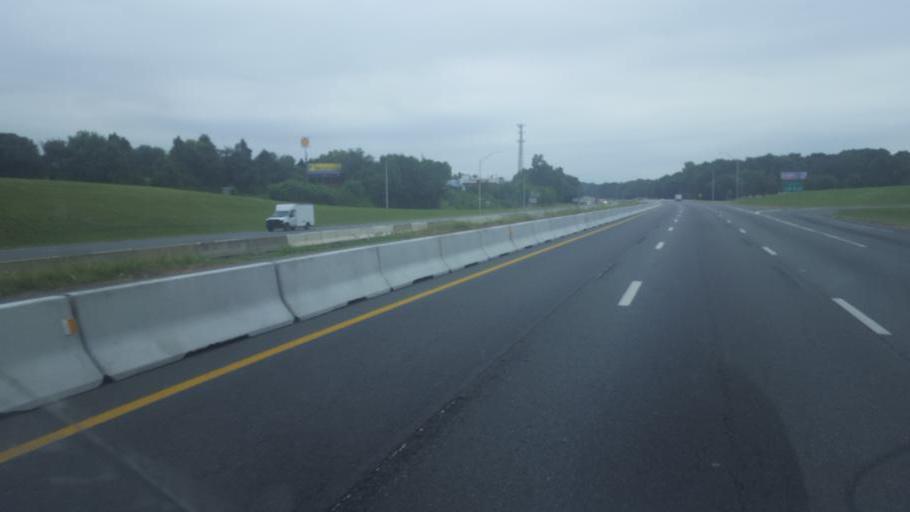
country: US
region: North Carolina
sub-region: Mecklenburg County
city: Charlotte
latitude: 35.3077
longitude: -80.8479
